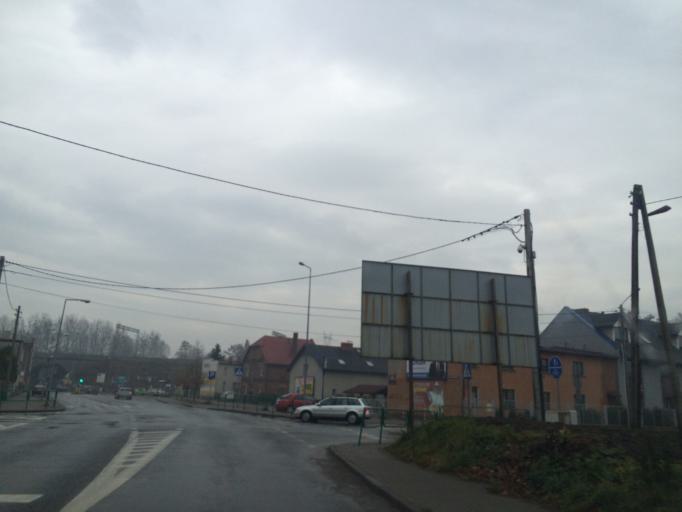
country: PL
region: Silesian Voivodeship
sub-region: Powiat tarnogorski
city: Radzionkow
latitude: 50.3963
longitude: 18.8967
